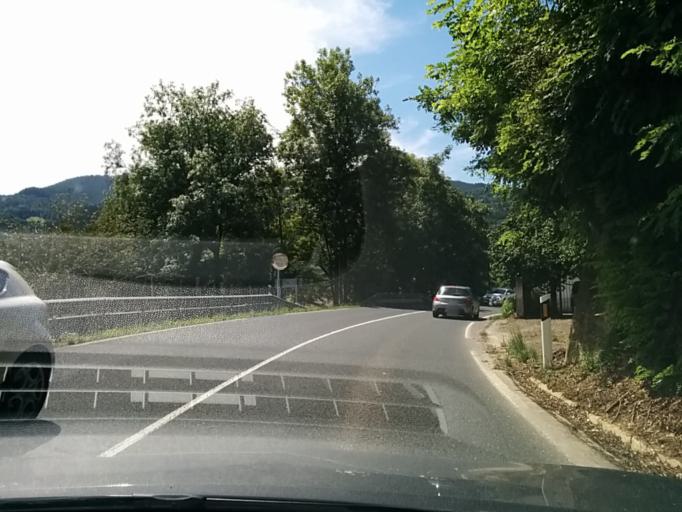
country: ES
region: Basque Country
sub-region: Provincia de Guipuzcoa
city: Usurbil
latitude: 43.2720
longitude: -2.0682
